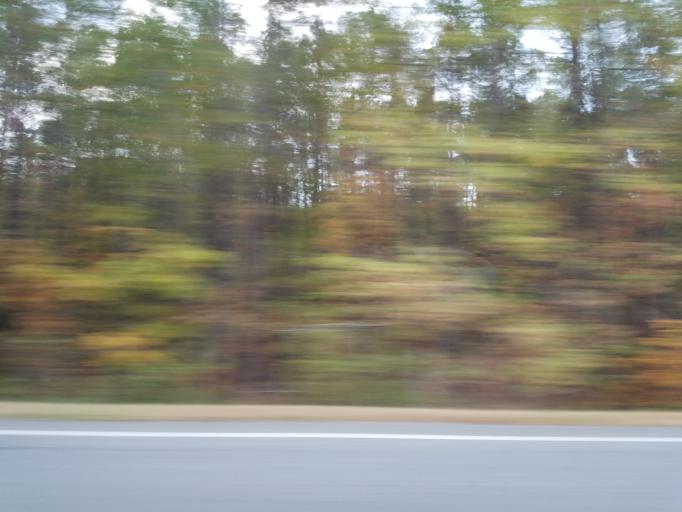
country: US
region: Georgia
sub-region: Murray County
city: Chatsworth
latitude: 34.5918
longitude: -84.6906
